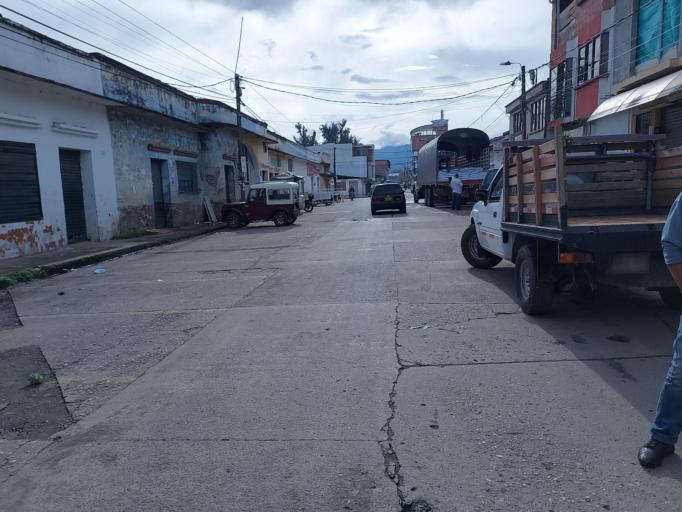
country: CO
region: Cauca
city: Rosas
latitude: 2.3529
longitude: -76.6846
